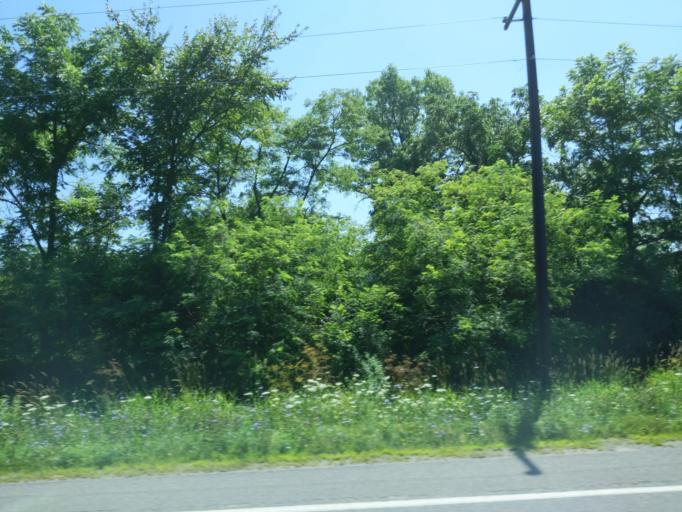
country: US
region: Wisconsin
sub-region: Vernon County
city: Westby
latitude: 43.6918
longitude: -91.0435
